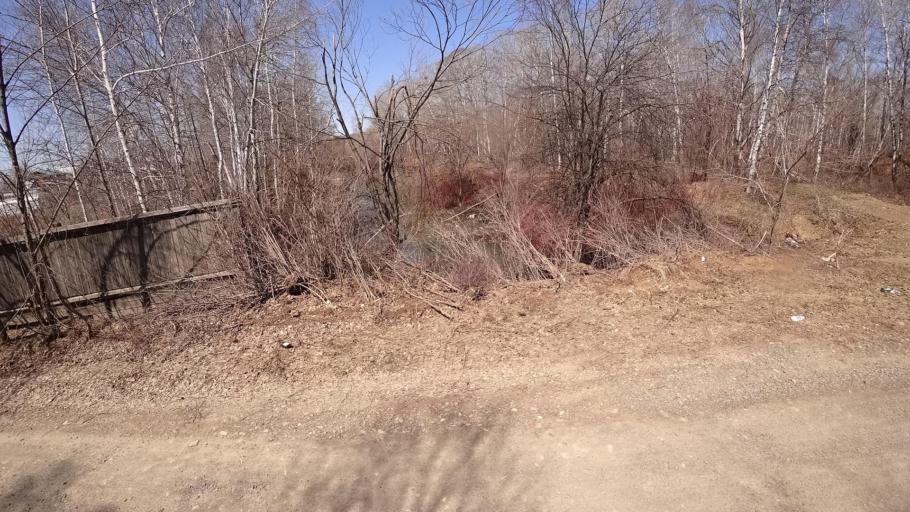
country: RU
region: Khabarovsk Krai
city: Khurba
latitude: 50.4137
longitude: 136.8711
